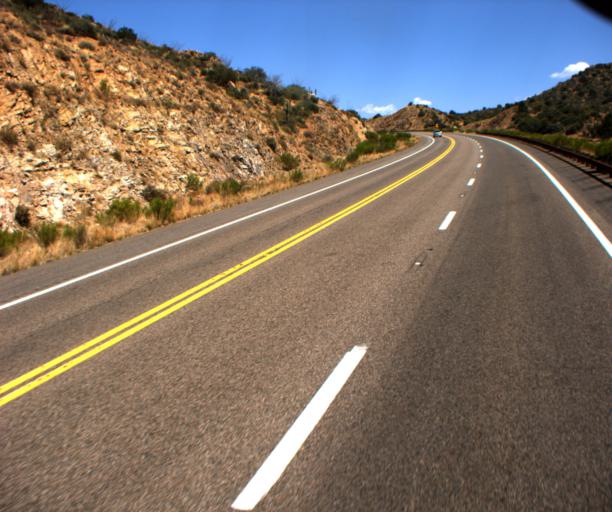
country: US
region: Arizona
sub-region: Gila County
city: Miami
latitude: 33.5397
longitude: -110.9363
